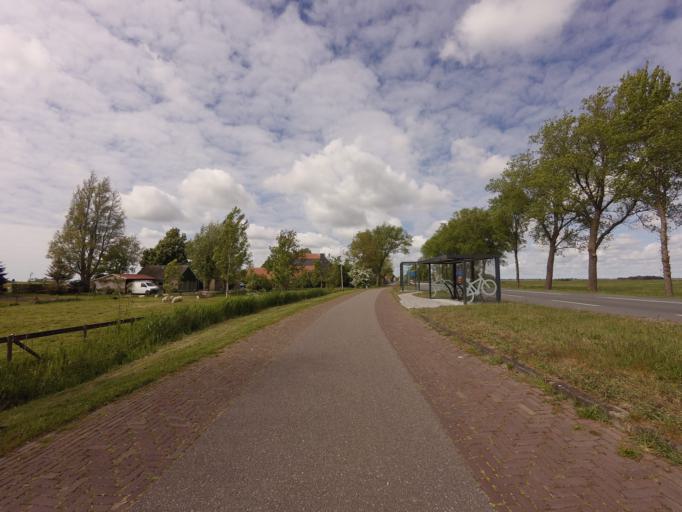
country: NL
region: Friesland
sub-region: Sudwest Fryslan
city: Woudsend
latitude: 52.9741
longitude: 5.6497
